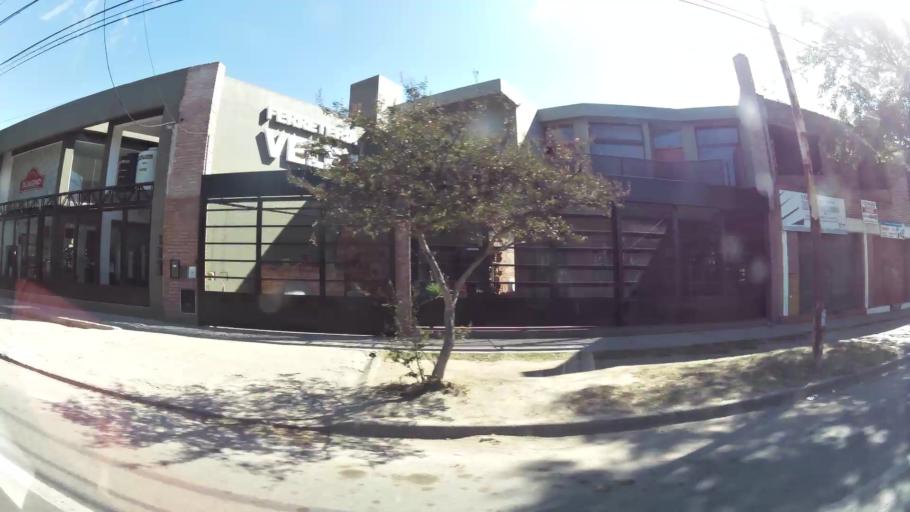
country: AR
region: Cordoba
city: Villa Allende
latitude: -31.3266
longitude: -64.2674
